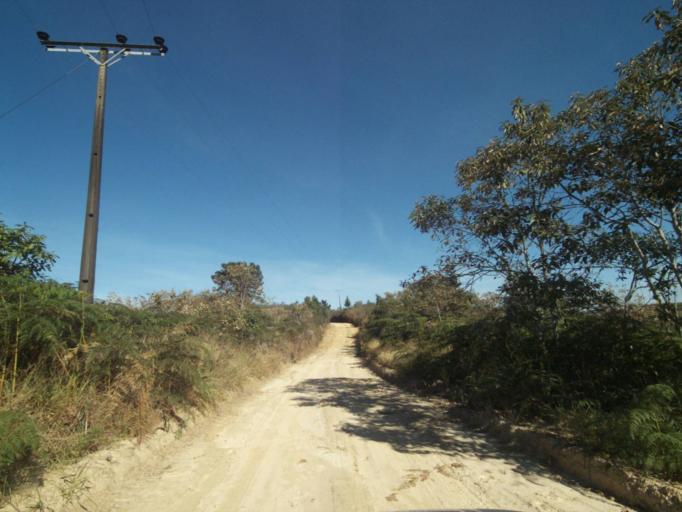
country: BR
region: Parana
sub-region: Tibagi
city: Tibagi
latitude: -24.5655
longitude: -50.4710
